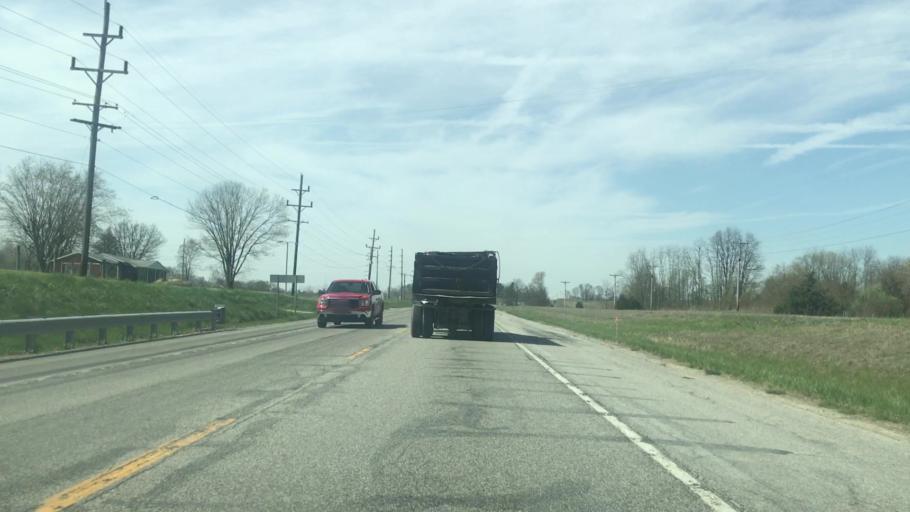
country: US
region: Indiana
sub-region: Putnam County
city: Cloverdale
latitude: 39.5568
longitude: -86.8120
